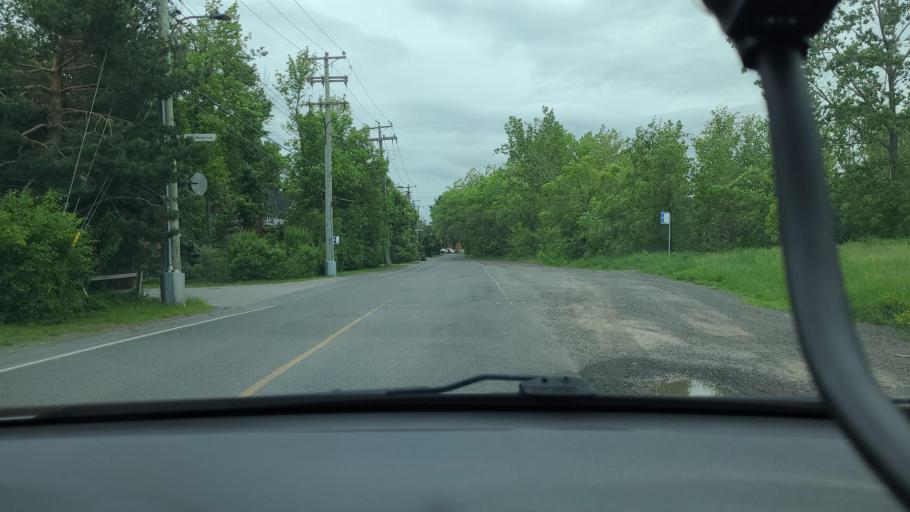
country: CA
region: Quebec
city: Montreal-Est
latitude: 45.6733
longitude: -73.5400
